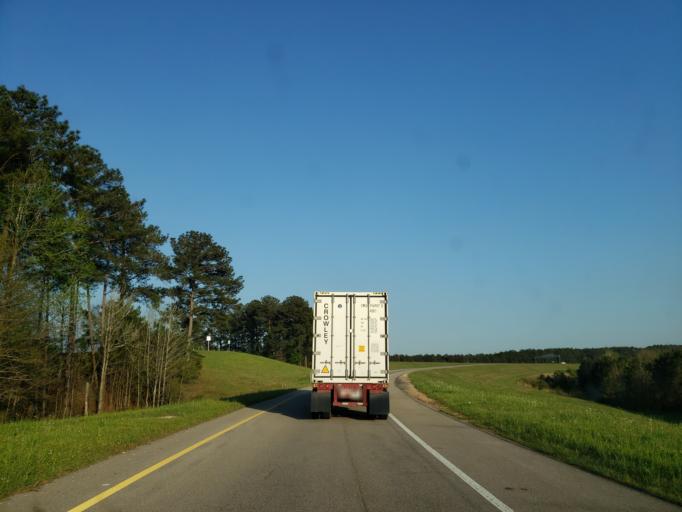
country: US
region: Mississippi
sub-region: Lauderdale County
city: Marion
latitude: 32.3819
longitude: -88.6392
